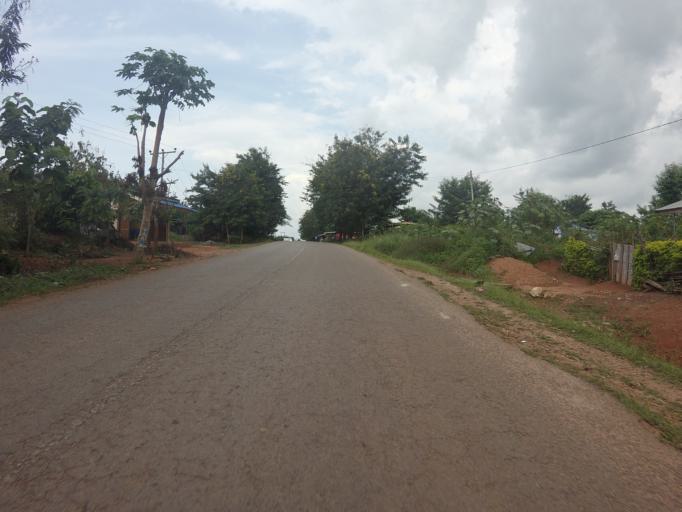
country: GH
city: Akropong
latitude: 5.9563
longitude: -0.1466
